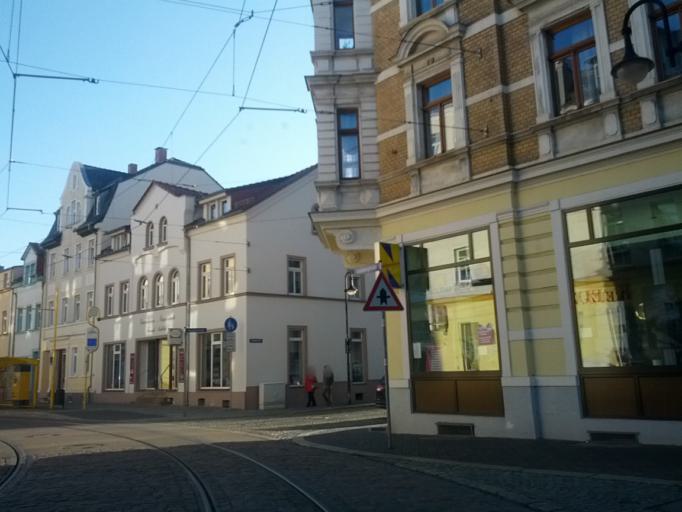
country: DE
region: Thuringia
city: Gera
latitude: 50.8847
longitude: 12.0688
